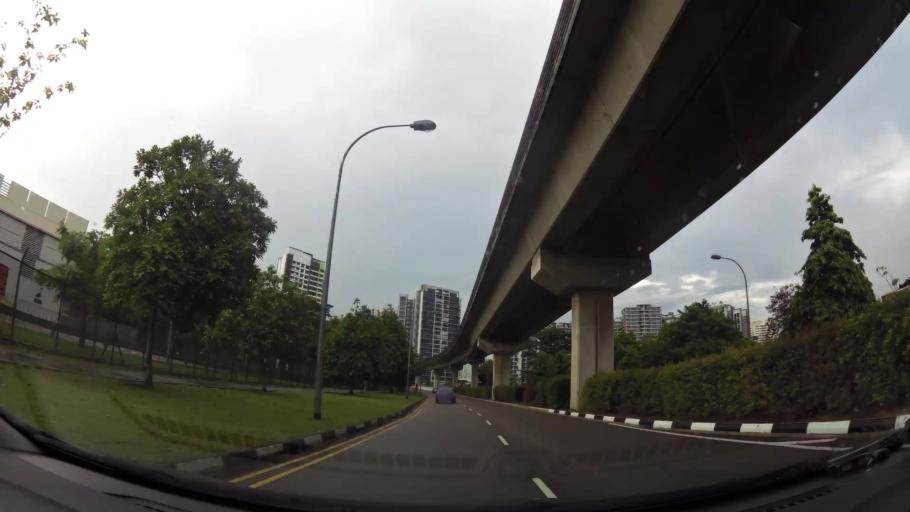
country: MY
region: Johor
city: Kampung Pasir Gudang Baru
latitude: 1.3912
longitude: 103.8829
